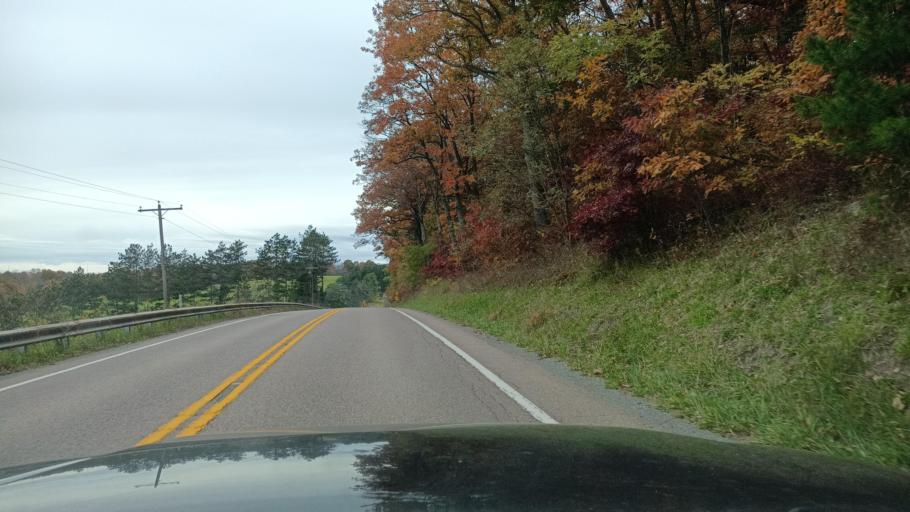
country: US
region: Maryland
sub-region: Garrett County
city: Oakland
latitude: 39.3001
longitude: -79.4419
